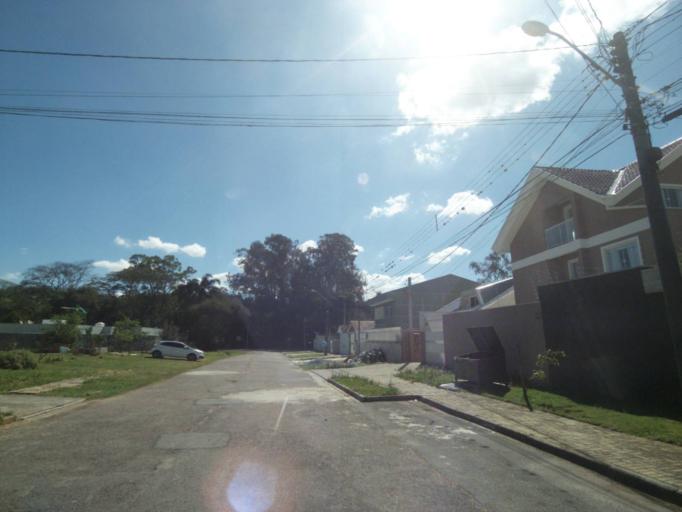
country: BR
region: Parana
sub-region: Curitiba
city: Curitiba
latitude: -25.3955
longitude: -49.2692
